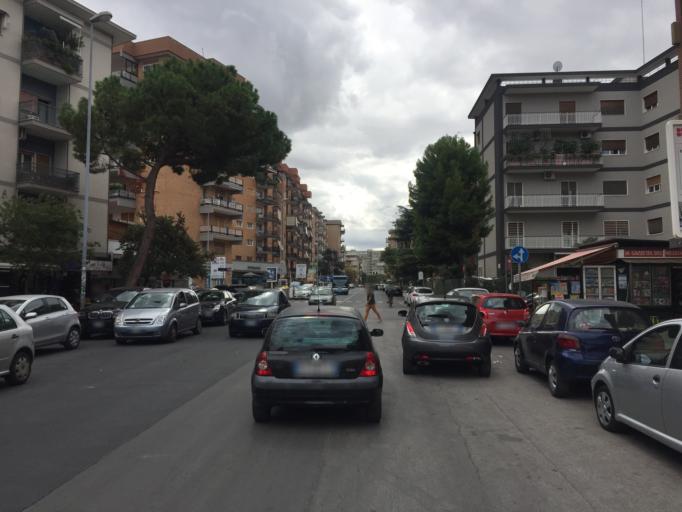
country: IT
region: Apulia
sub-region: Provincia di Bari
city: Bari
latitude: 41.1039
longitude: 16.8596
